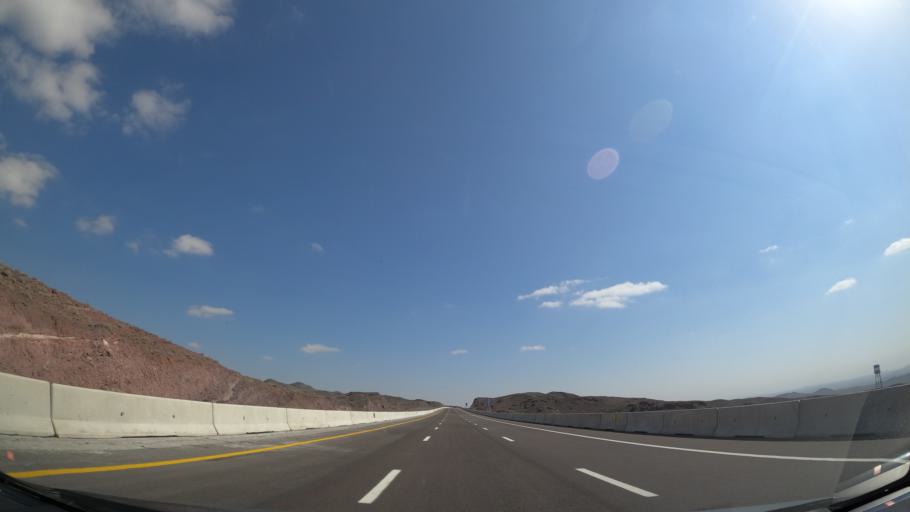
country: IR
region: Alborz
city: Eshtehard
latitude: 35.6624
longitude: 50.6535
